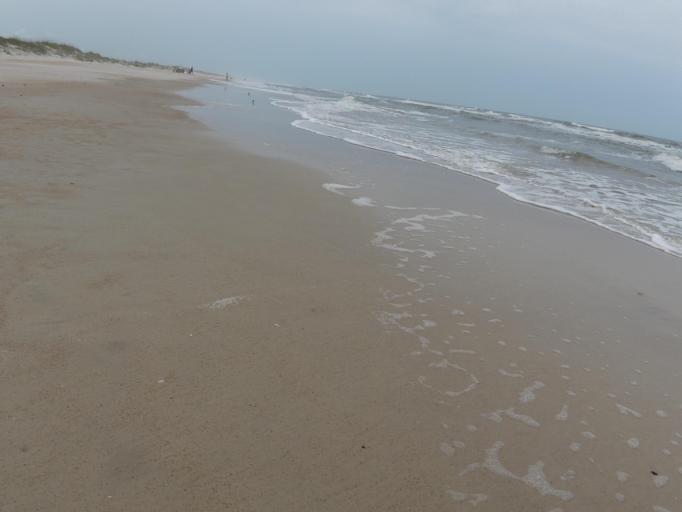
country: US
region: Florida
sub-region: Saint Johns County
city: Saint Augustine Beach
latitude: 29.8890
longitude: -81.2741
